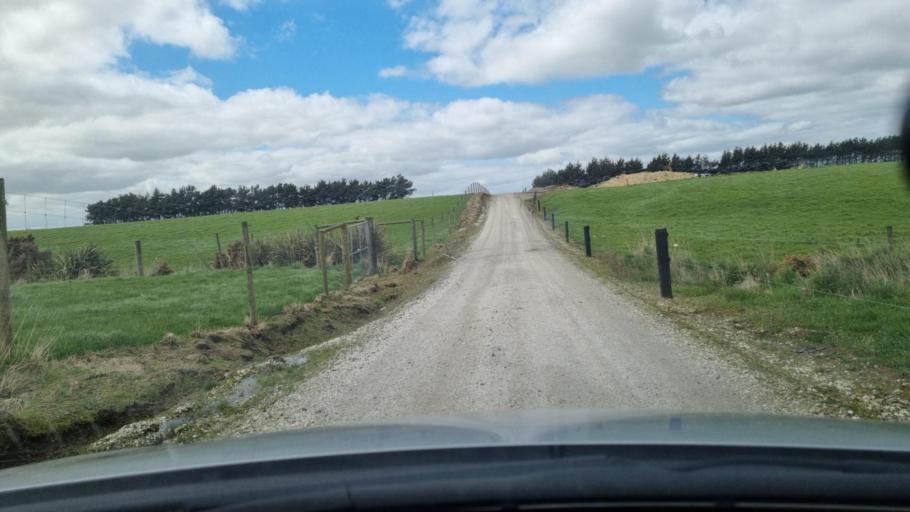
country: NZ
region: Southland
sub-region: Invercargill City
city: Invercargill
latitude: -46.4557
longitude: 168.4221
